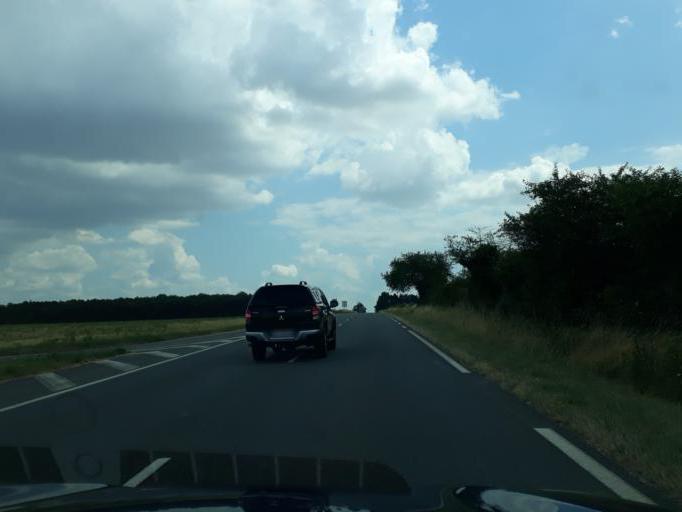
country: FR
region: Centre
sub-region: Departement du Cher
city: Avord
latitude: 47.0346
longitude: 2.6237
